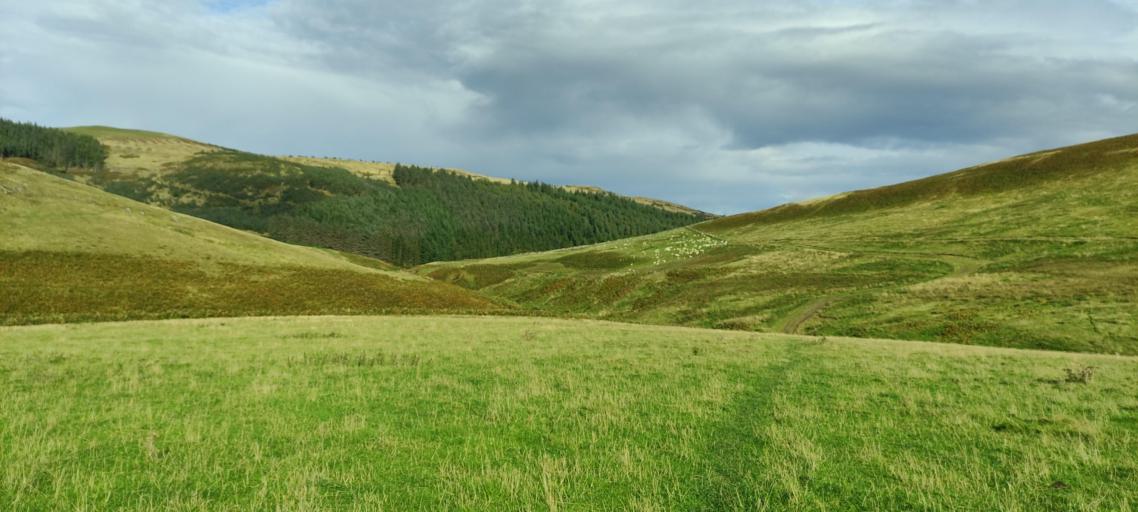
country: GB
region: England
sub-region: Northumberland
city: Kirknewton
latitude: 55.5451
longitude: -2.2109
